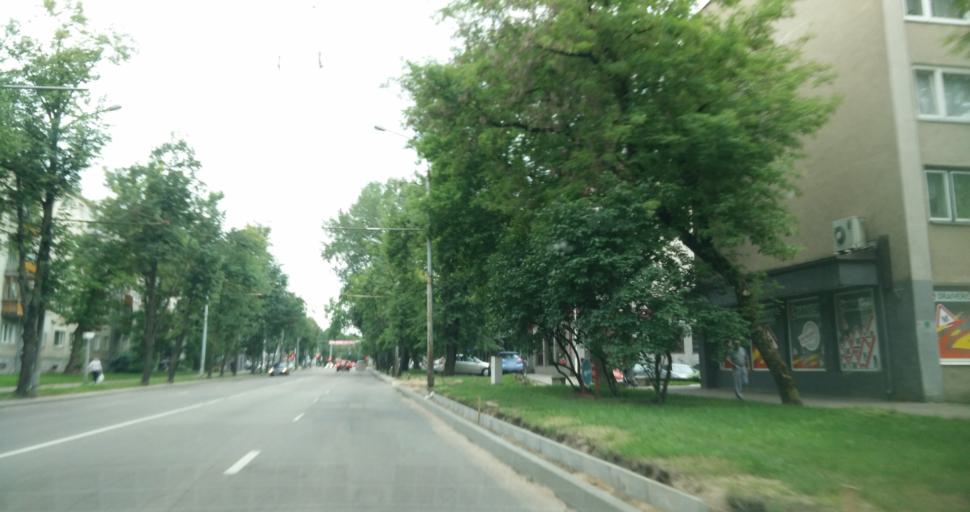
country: LT
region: Vilnius County
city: Rasos
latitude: 54.7136
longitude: 25.3154
